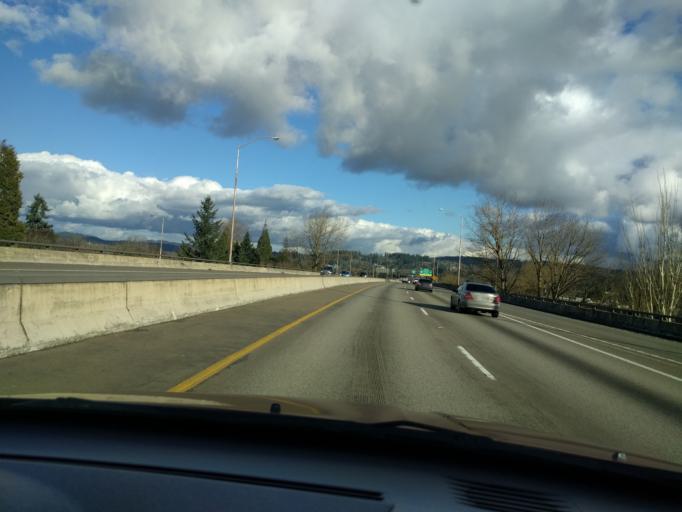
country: US
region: Oregon
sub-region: Clackamas County
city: West Linn
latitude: 45.3628
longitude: -122.6101
